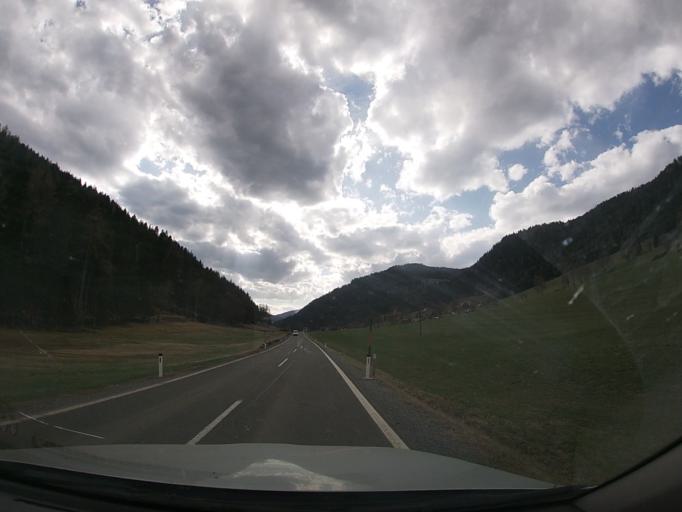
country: AT
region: Styria
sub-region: Politischer Bezirk Murau
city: Sankt Lambrecht
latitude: 47.0663
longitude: 14.2665
